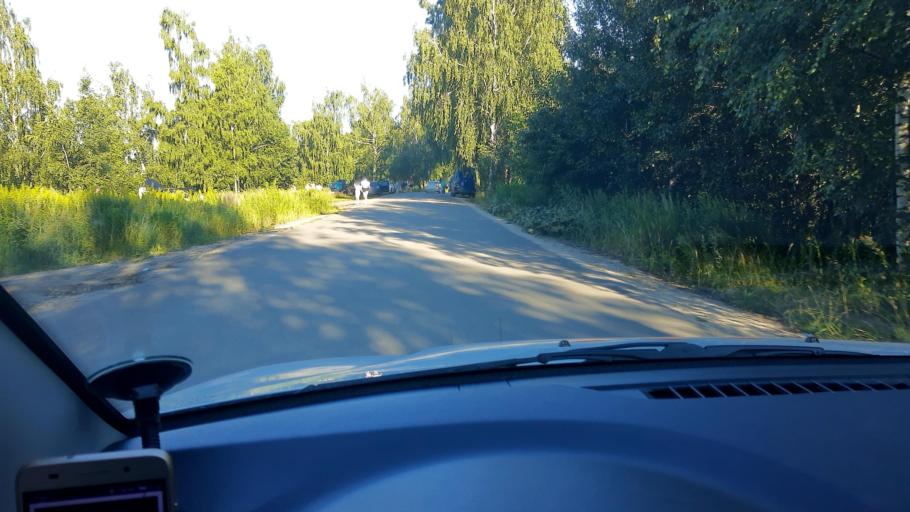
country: RU
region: Nizjnij Novgorod
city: Gorbatovka
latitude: 56.3642
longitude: 43.7823
